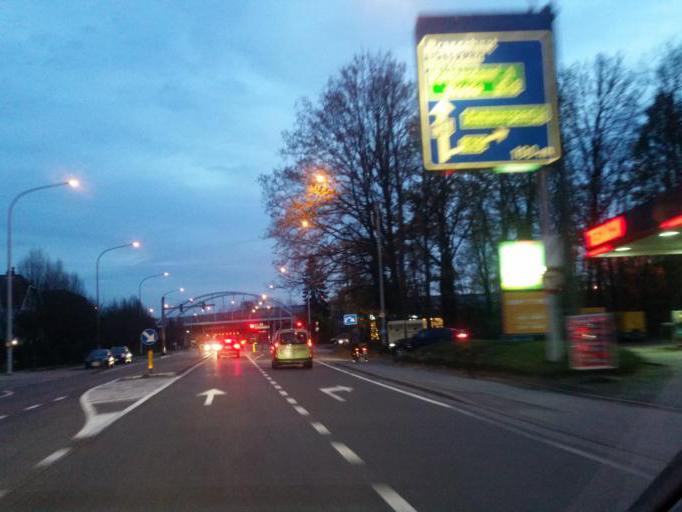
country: BE
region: Flanders
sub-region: Provincie Antwerpen
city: Brasschaat
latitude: 51.2711
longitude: 4.4589
